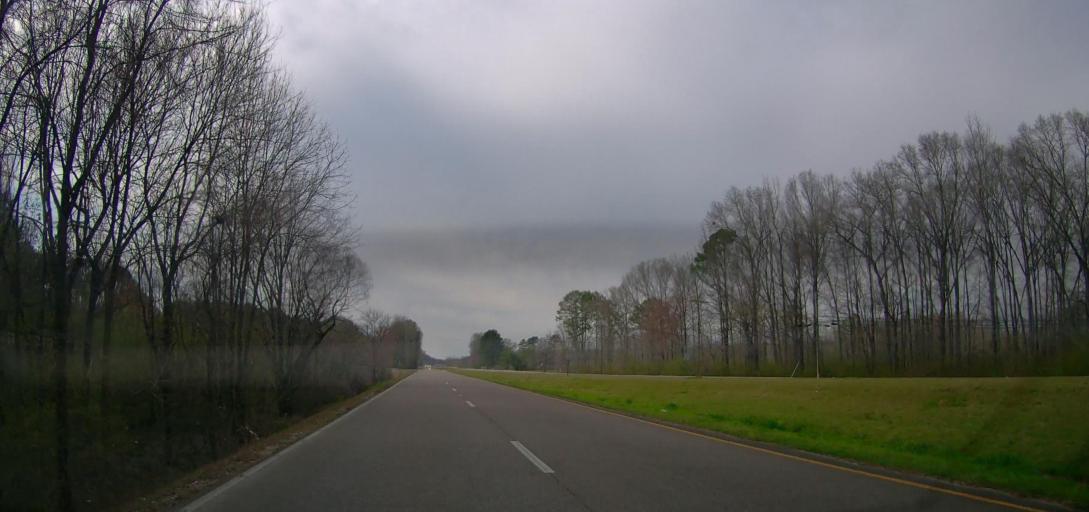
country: US
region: Alabama
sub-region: Walker County
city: Carbon Hill
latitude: 33.8795
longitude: -87.5037
